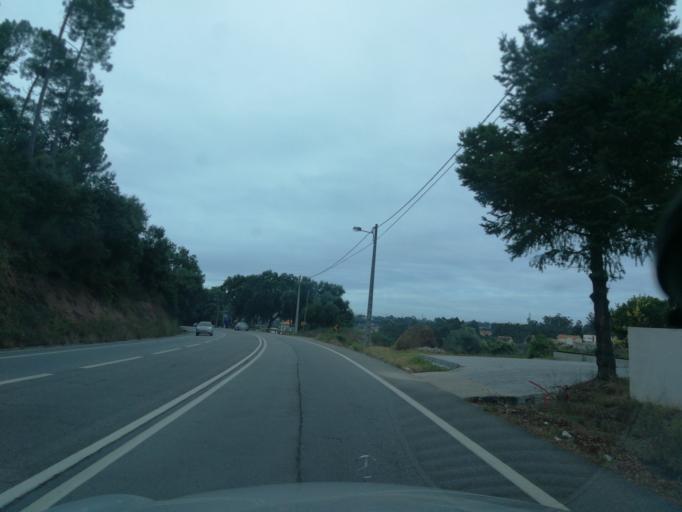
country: PT
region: Aveiro
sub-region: Agueda
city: Agueda
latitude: 40.5834
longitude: -8.4503
